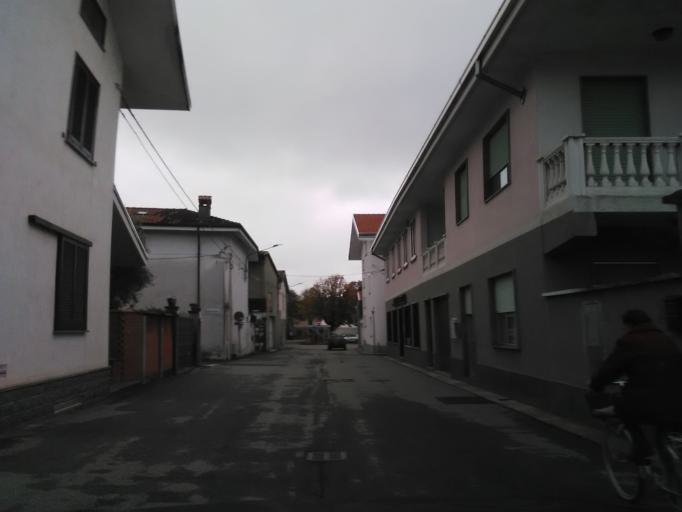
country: IT
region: Piedmont
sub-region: Provincia di Torino
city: Villareggia
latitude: 45.3113
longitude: 7.9770
